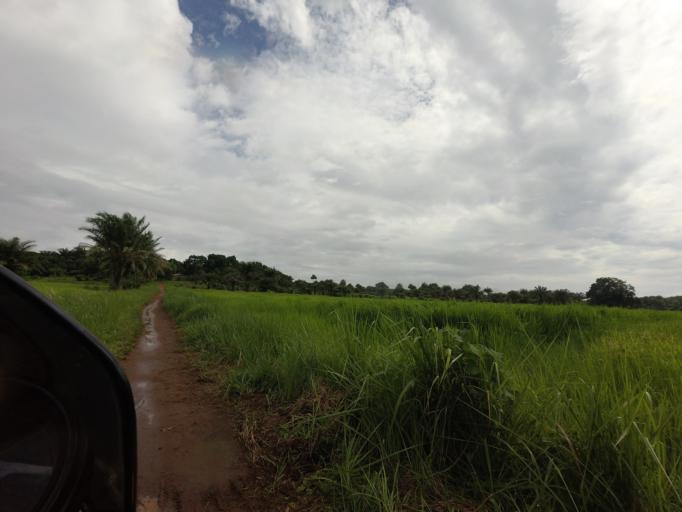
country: SL
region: Northern Province
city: Mambolo
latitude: 9.0013
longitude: -12.9646
